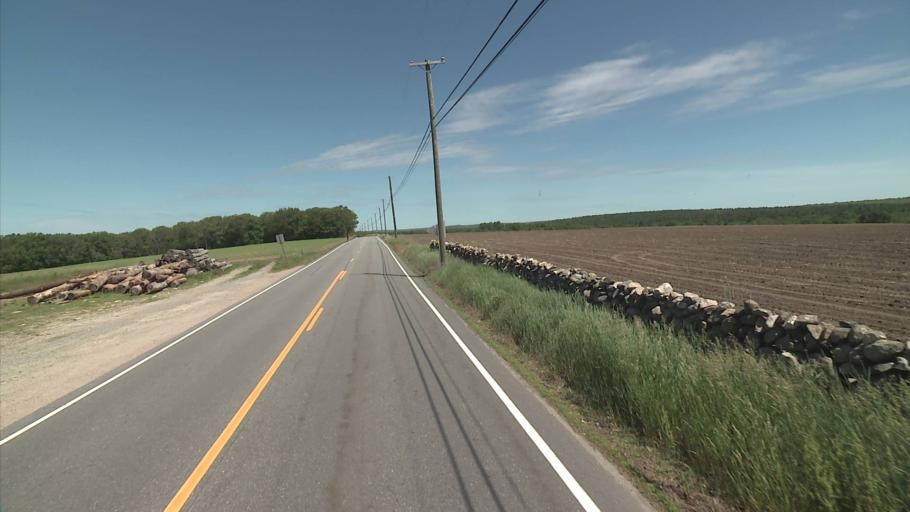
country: US
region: Rhode Island
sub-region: Washington County
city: Hopkinton
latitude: 41.5395
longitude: -71.8400
